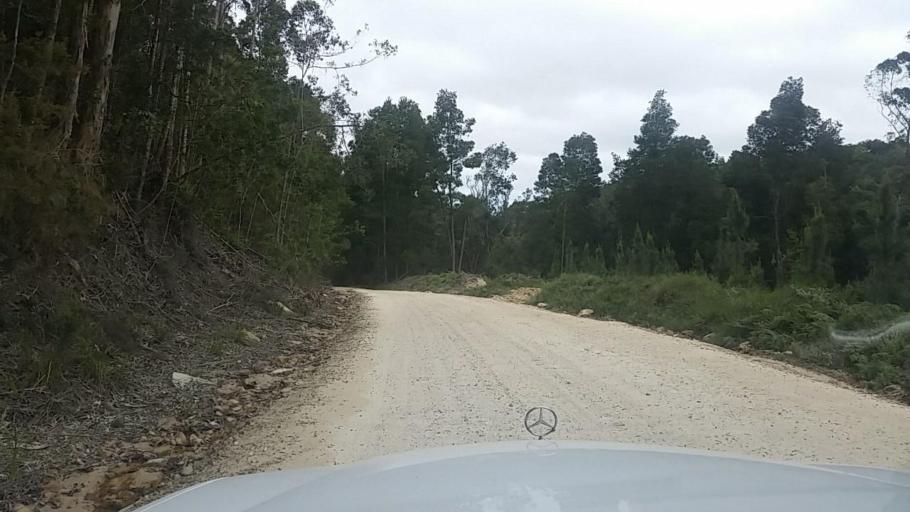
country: ZA
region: Western Cape
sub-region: Eden District Municipality
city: Knysna
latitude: -33.9991
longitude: 23.1155
